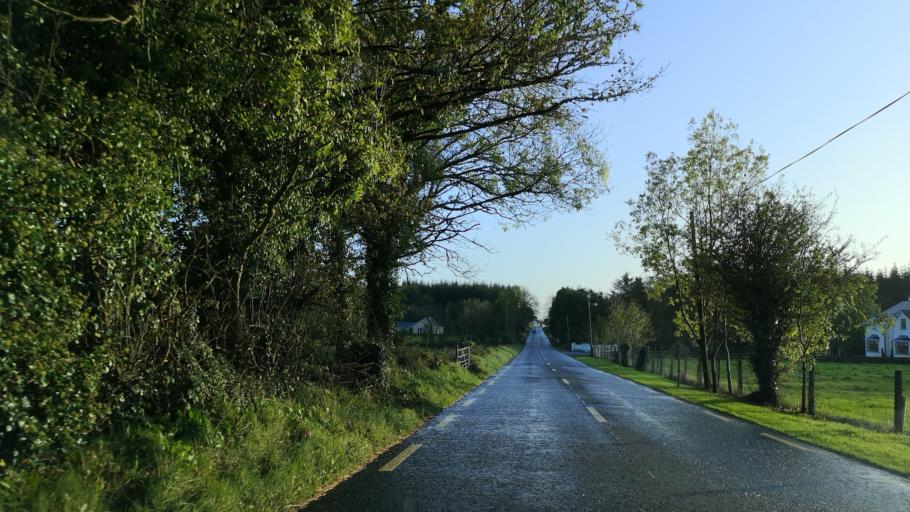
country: IE
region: Connaught
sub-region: Roscommon
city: Castlerea
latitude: 53.7220
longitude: -8.5591
